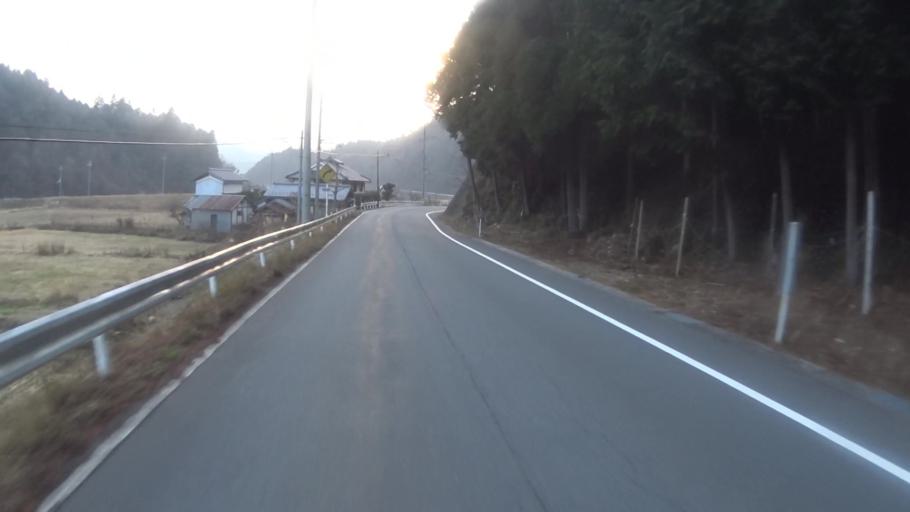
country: JP
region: Kyoto
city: Maizuru
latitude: 35.3798
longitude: 135.4481
